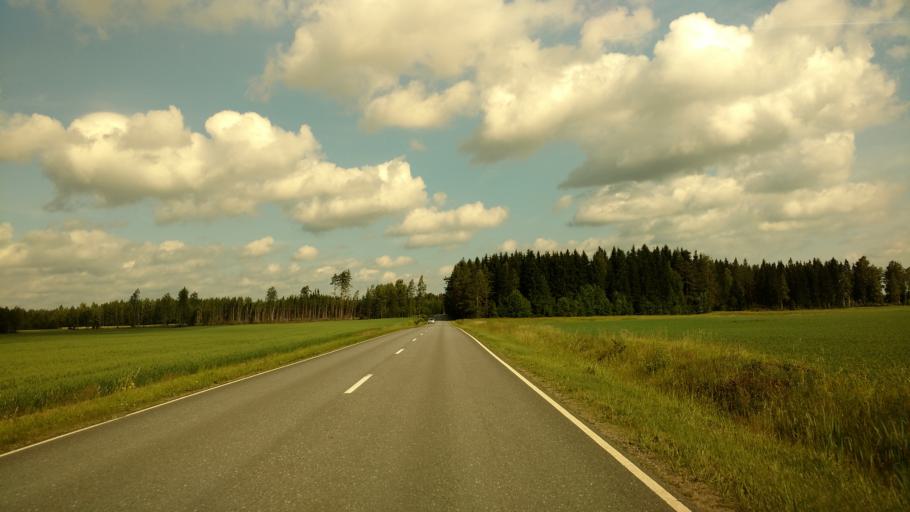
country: FI
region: Varsinais-Suomi
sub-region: Loimaa
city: Koski Tl
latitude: 60.6167
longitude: 23.1157
